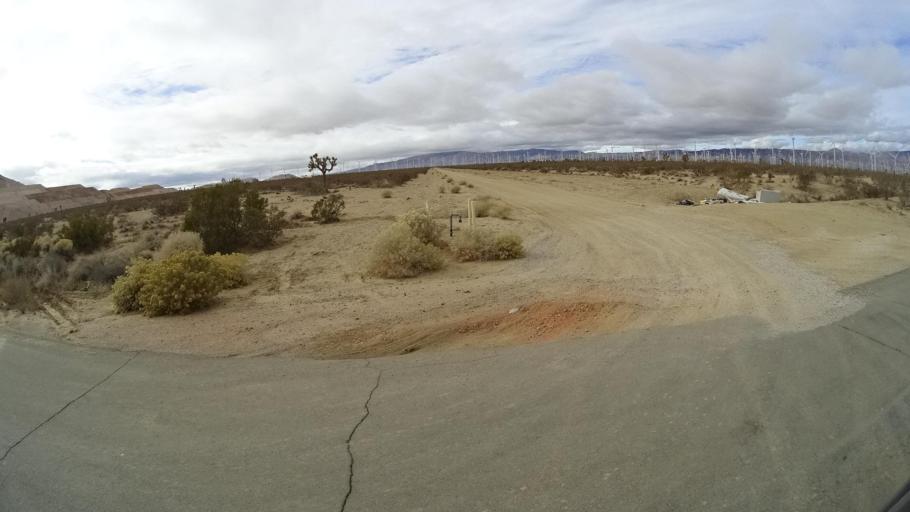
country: US
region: California
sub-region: Kern County
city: Mojave
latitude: 35.0020
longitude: -118.1857
